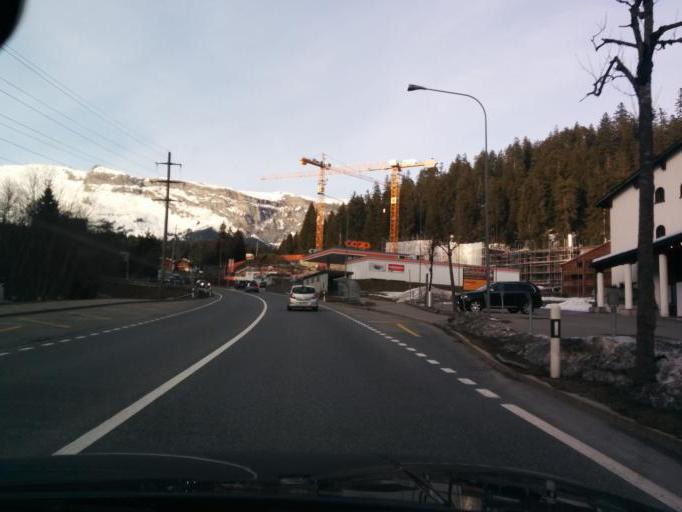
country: CH
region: Grisons
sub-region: Surselva District
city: Laax
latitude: 46.8154
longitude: 9.2662
